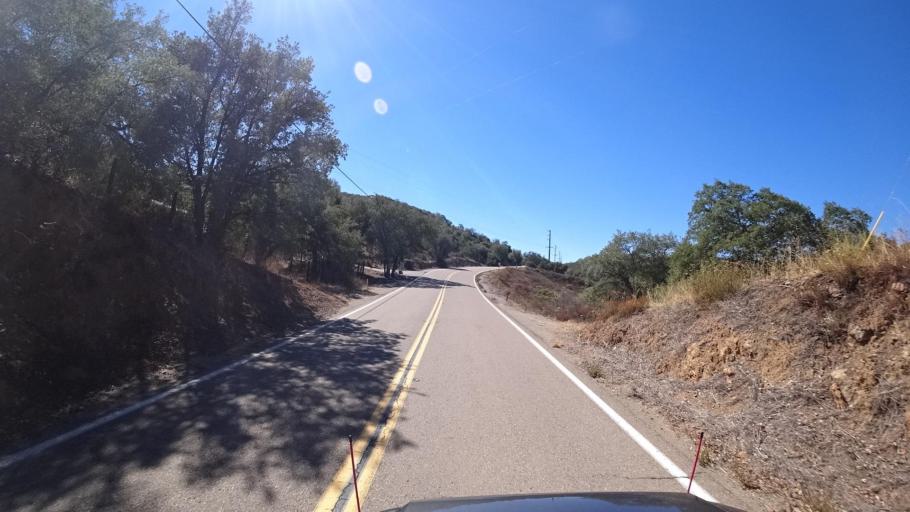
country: US
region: California
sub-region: San Diego County
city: Descanso
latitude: 32.7866
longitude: -116.6645
